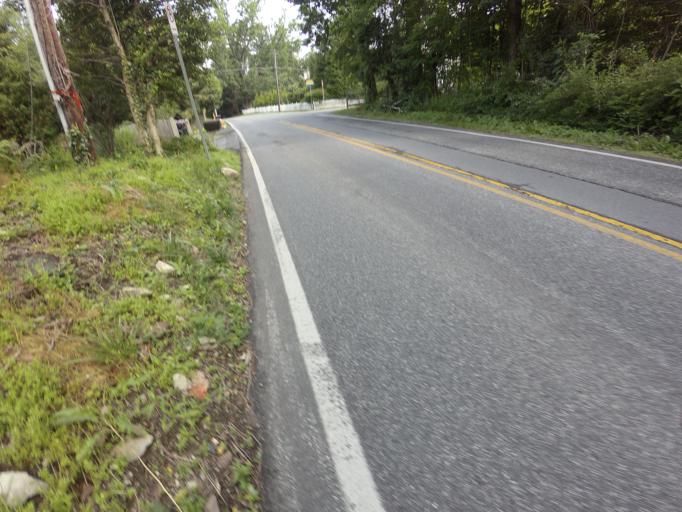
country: US
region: Maryland
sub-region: Baltimore County
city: Lutherville
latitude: 39.3940
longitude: -76.6432
